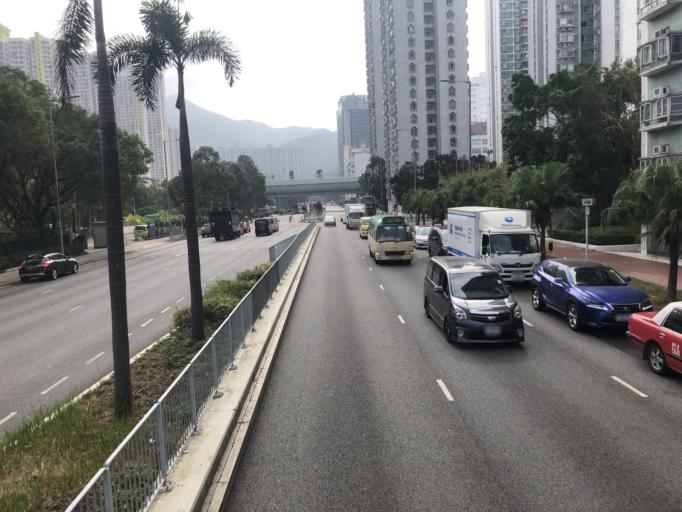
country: HK
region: Sha Tin
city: Sha Tin
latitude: 22.3875
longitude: 114.2048
